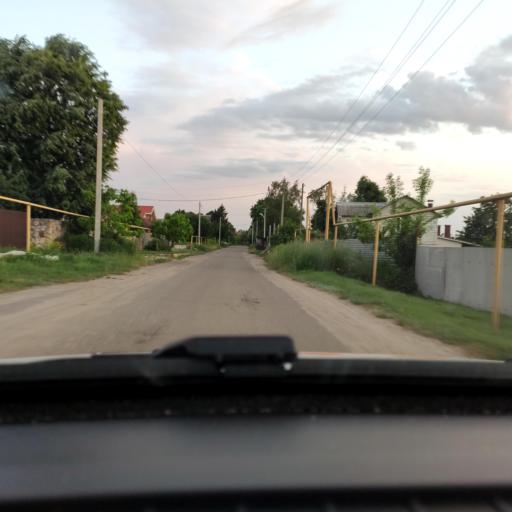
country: RU
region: Voronezj
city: Semiluki
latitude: 51.7460
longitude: 39.0194
